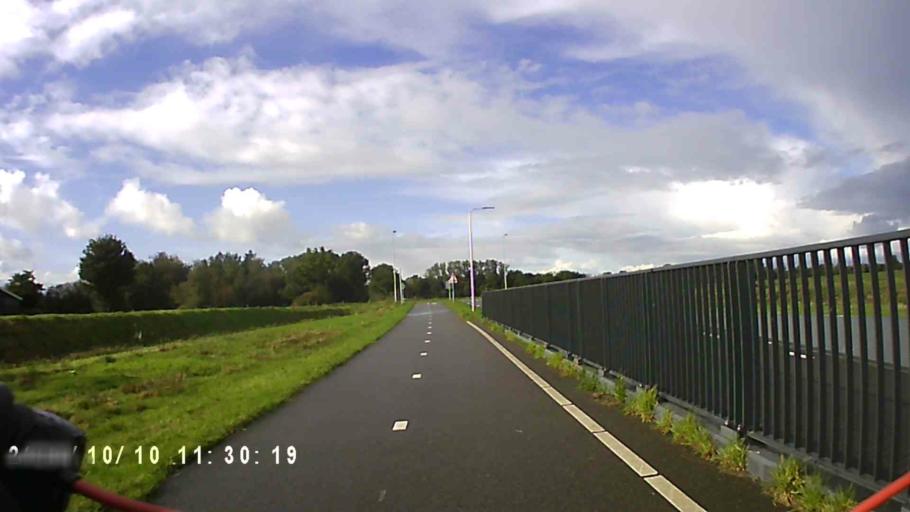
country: NL
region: Friesland
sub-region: Gemeente Smallingerland
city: Drachtstercompagnie
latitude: 53.0859
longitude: 6.1435
